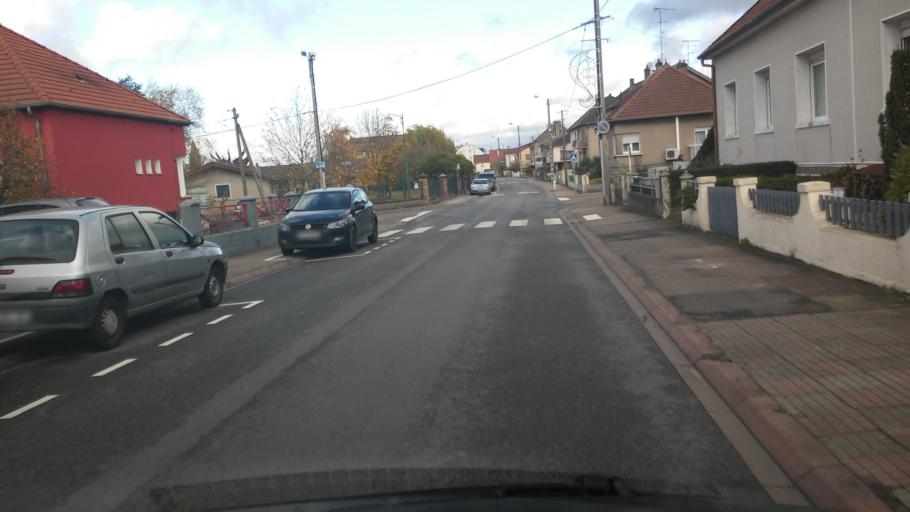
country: FR
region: Lorraine
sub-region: Departement de la Moselle
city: Talange
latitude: 49.2332
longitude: 6.1767
